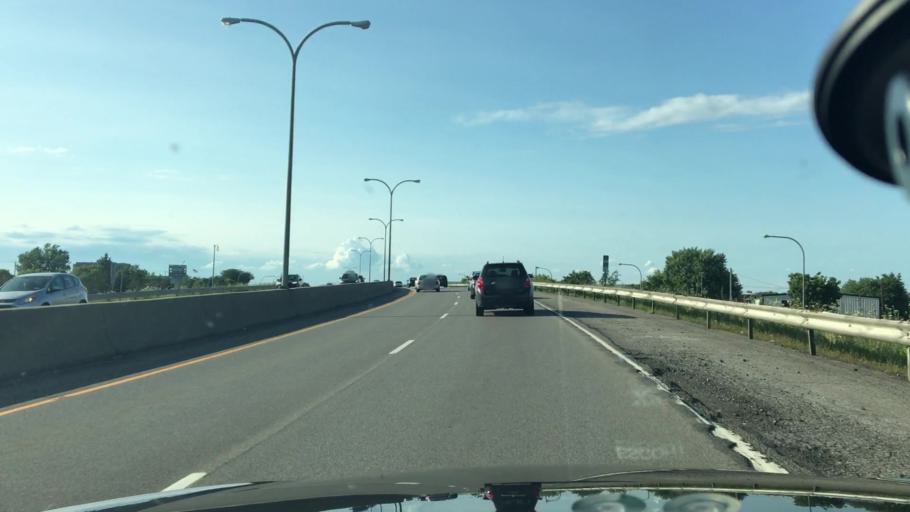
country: US
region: New York
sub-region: Erie County
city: Lackawanna
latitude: 42.8263
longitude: -78.8500
